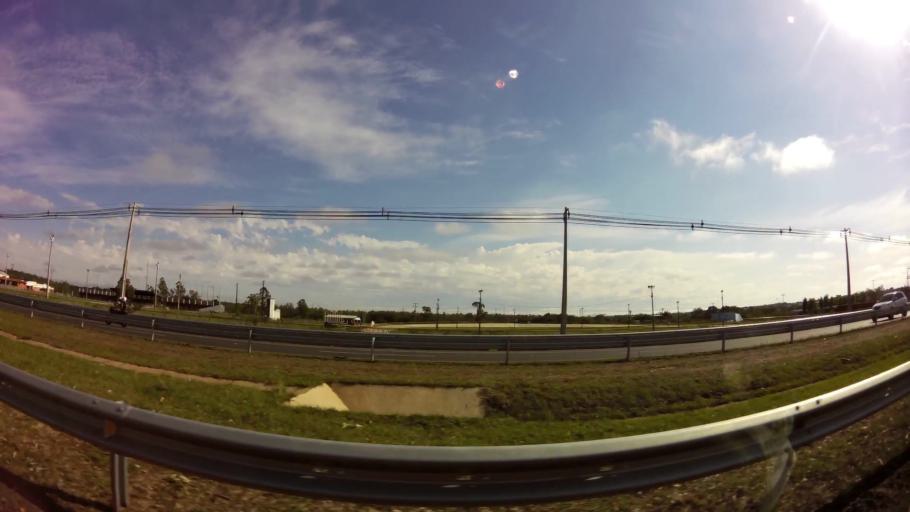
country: PY
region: Central
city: Fernando de la Mora
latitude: -25.2606
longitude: -57.5286
